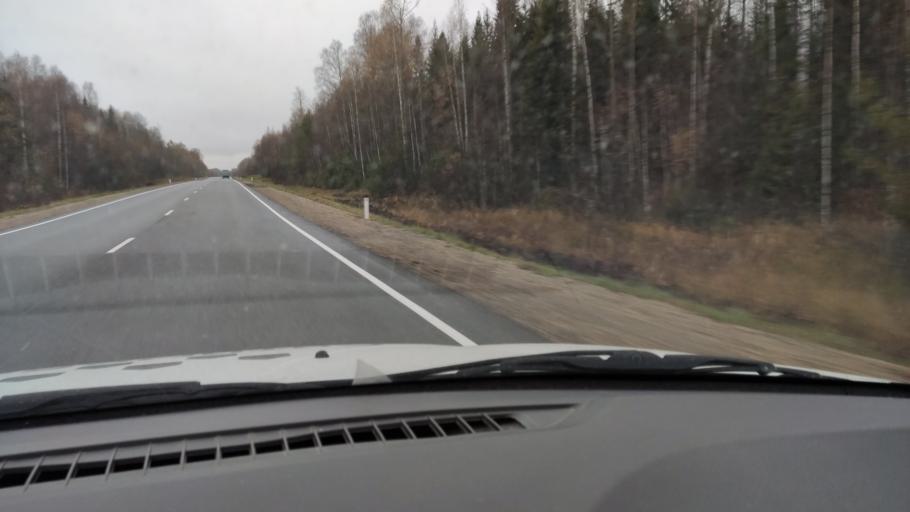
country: RU
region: Kirov
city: Chernaya Kholunitsa
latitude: 58.7810
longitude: 51.9138
